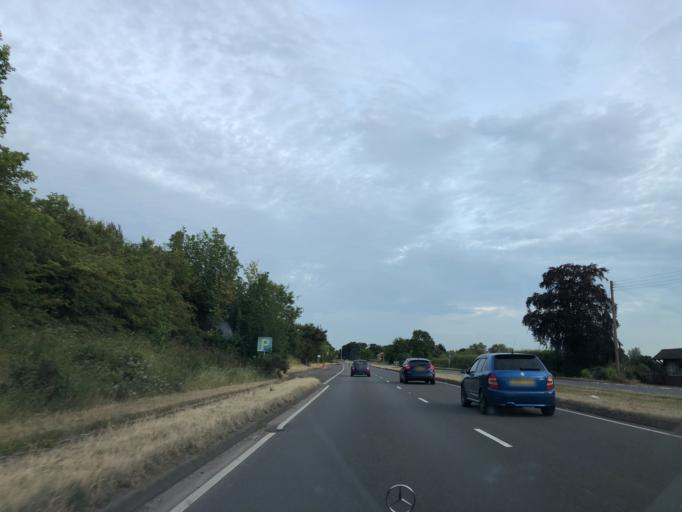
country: GB
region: England
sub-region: Solihull
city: Barston
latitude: 52.4169
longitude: -1.6763
